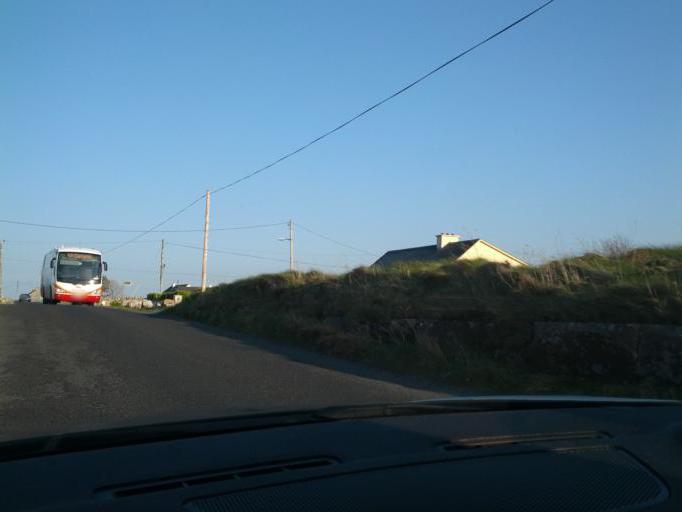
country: IE
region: Connaught
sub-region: County Galway
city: Oughterard
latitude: 53.2443
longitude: -9.5236
